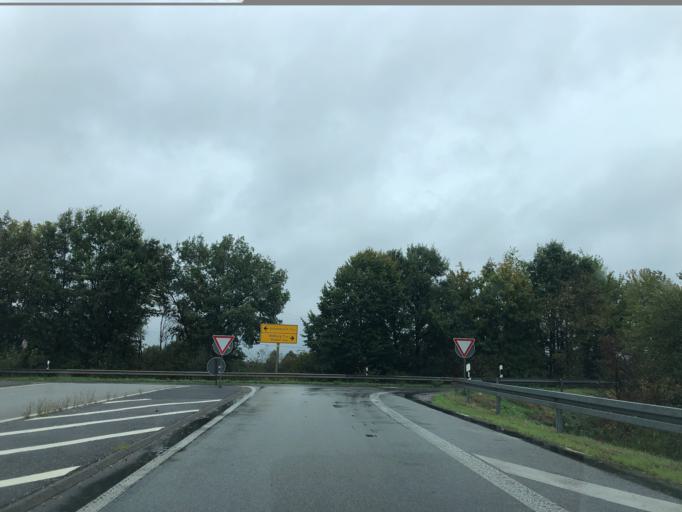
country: DE
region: North Rhine-Westphalia
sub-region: Regierungsbezirk Dusseldorf
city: Grevenbroich
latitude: 51.0866
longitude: 6.5532
